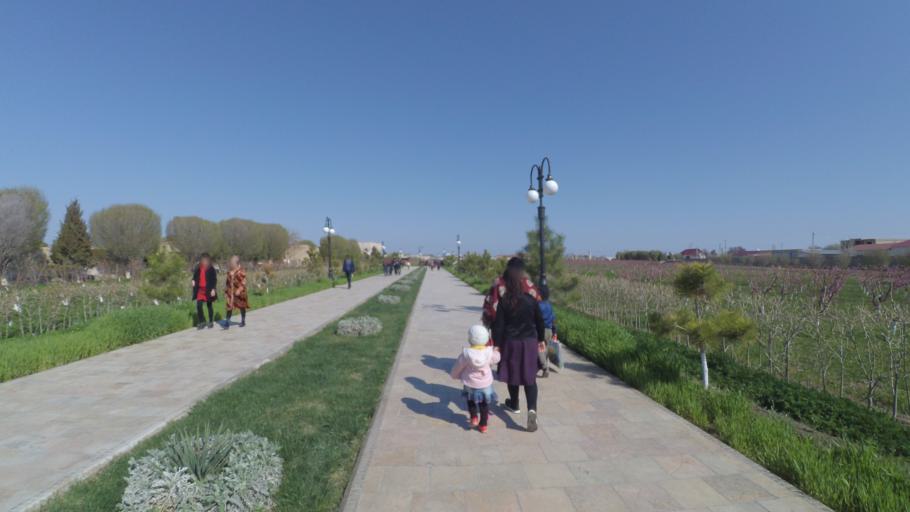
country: UZ
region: Bukhara
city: Kogon
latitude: 39.8010
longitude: 64.5388
